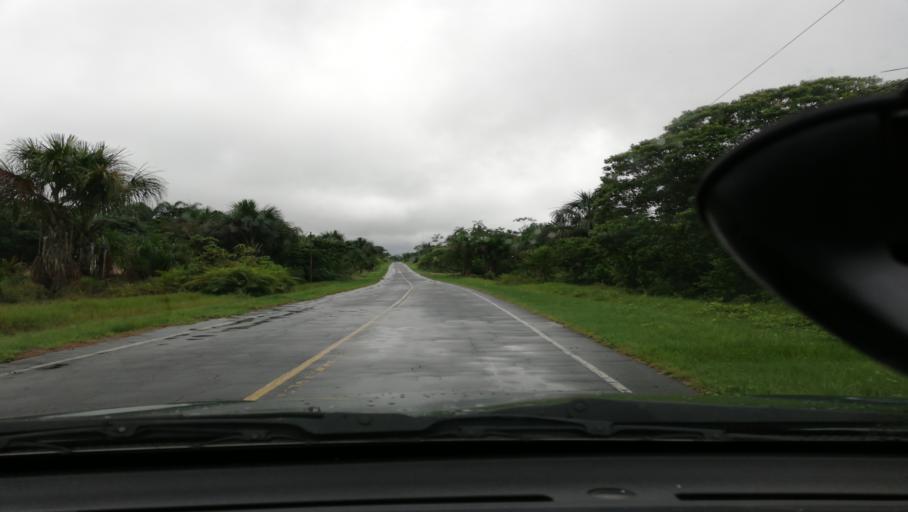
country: PE
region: Loreto
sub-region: Provincia de Loreto
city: Nauta
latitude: -4.2505
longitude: -73.4954
